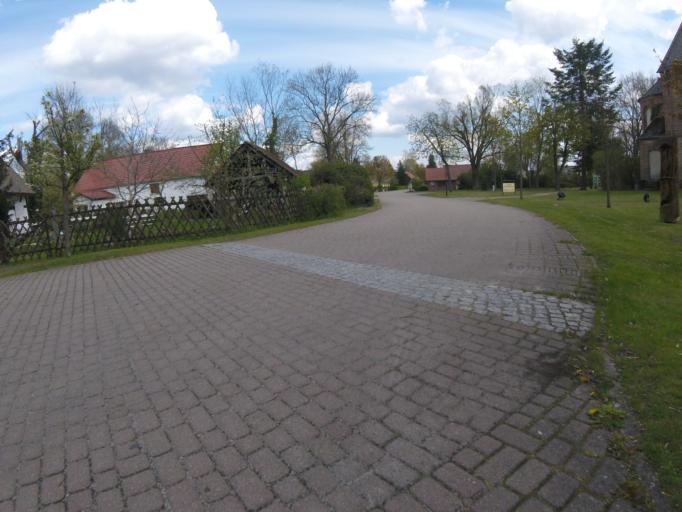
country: DE
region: Brandenburg
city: Munchehofe
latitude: 52.2233
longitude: 13.7661
